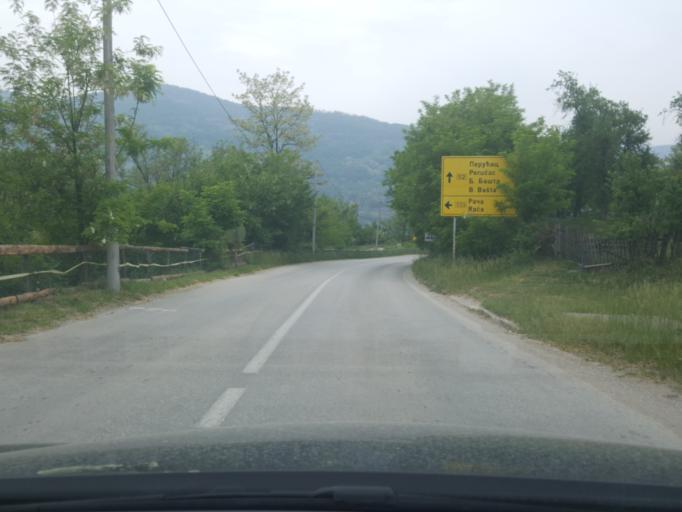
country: RS
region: Central Serbia
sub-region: Zlatiborski Okrug
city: Bajina Basta
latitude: 43.9660
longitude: 19.5496
